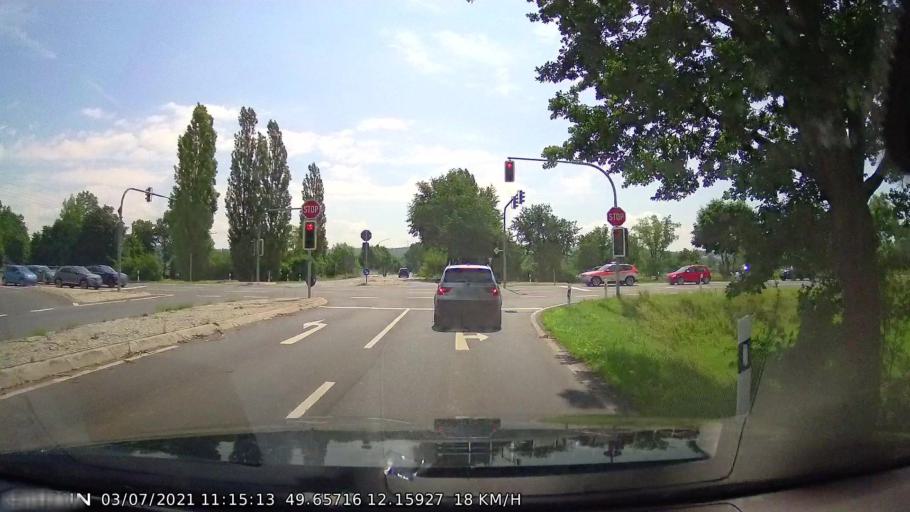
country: DE
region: Bavaria
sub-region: Upper Palatinate
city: Schirmitz
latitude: 49.6571
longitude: 12.1593
